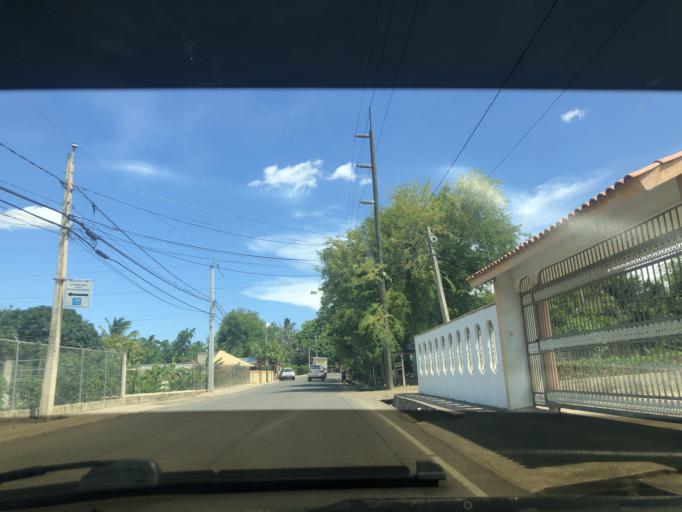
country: DO
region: Santiago
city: Santiago de los Caballeros
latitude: 19.4008
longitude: -70.6698
